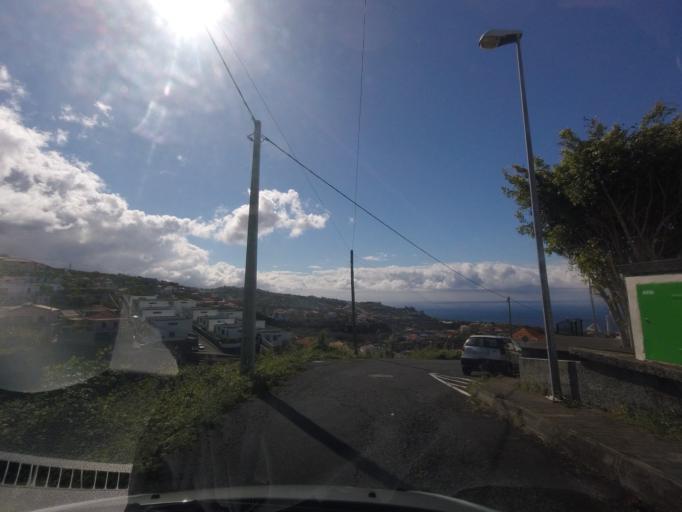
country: PT
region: Madeira
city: Camara de Lobos
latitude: 32.6606
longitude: -16.9730
